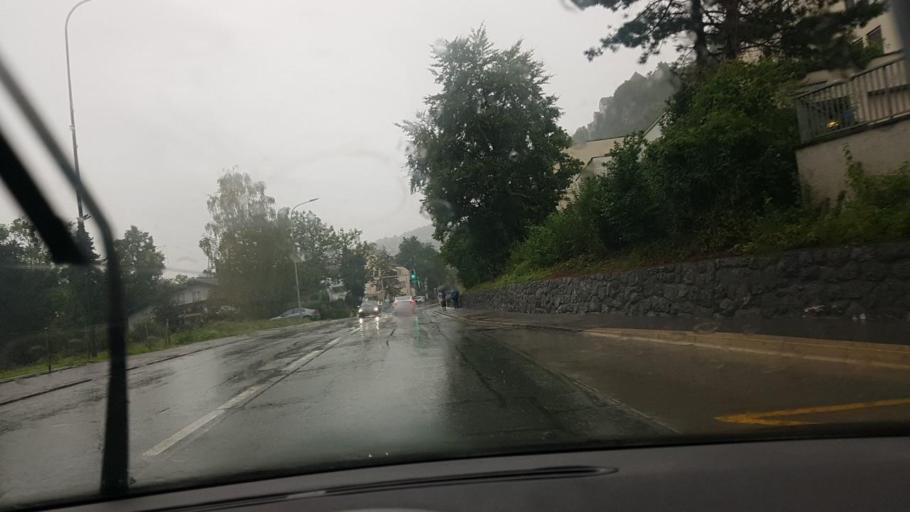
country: LI
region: Vaduz
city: Vaduz
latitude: 47.1341
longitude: 9.5221
